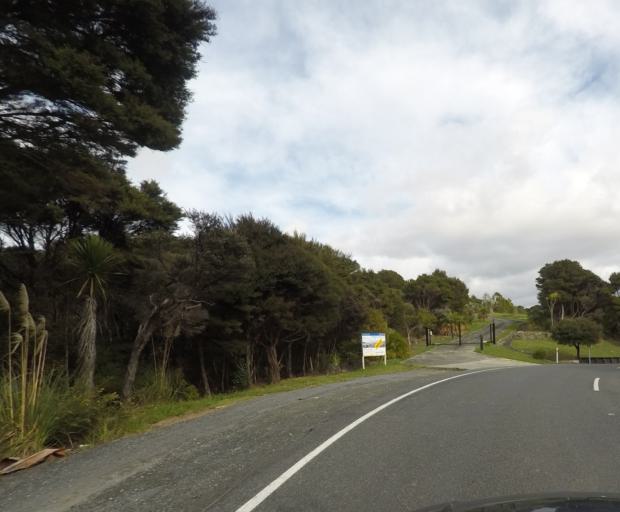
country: NZ
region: Northland
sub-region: Whangarei
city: Ruakaka
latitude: -36.0608
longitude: 174.5678
